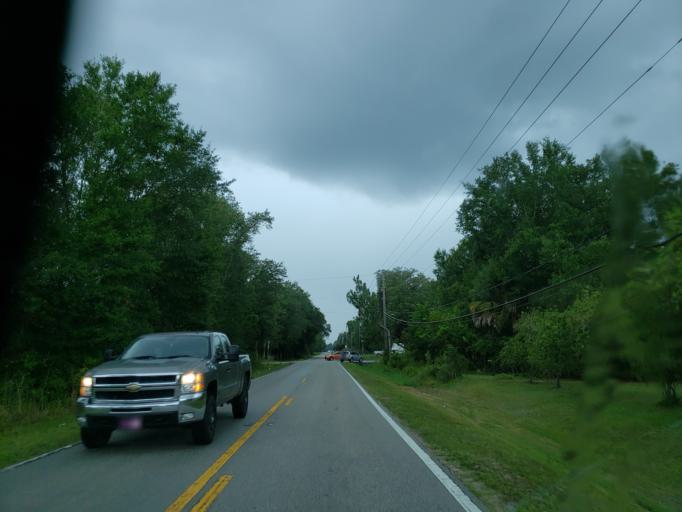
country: US
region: Florida
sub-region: Pasco County
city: Wesley Chapel
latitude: 28.2614
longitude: -82.3580
